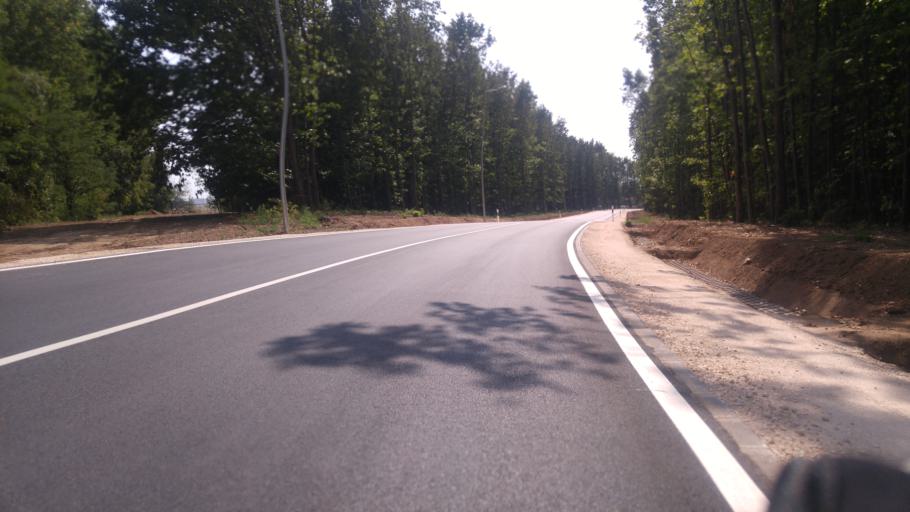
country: HU
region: Budapest
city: Budapest XVII. keruelet
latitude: 47.4516
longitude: 19.2440
